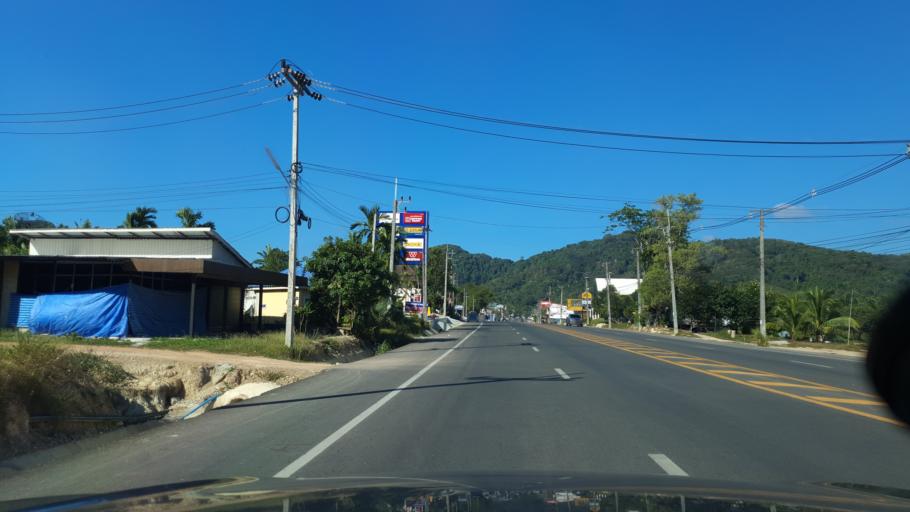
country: TH
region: Phangnga
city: Ban Ao Nang
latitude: 8.0421
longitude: 98.8457
